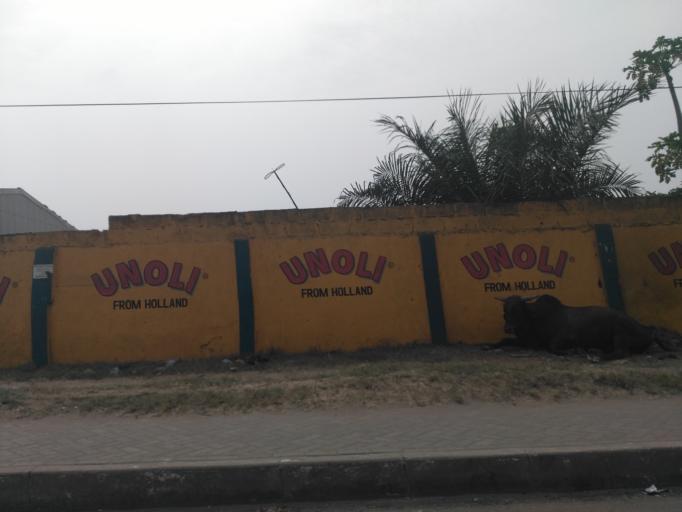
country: GH
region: Greater Accra
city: Accra
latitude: 5.5393
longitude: -0.2183
